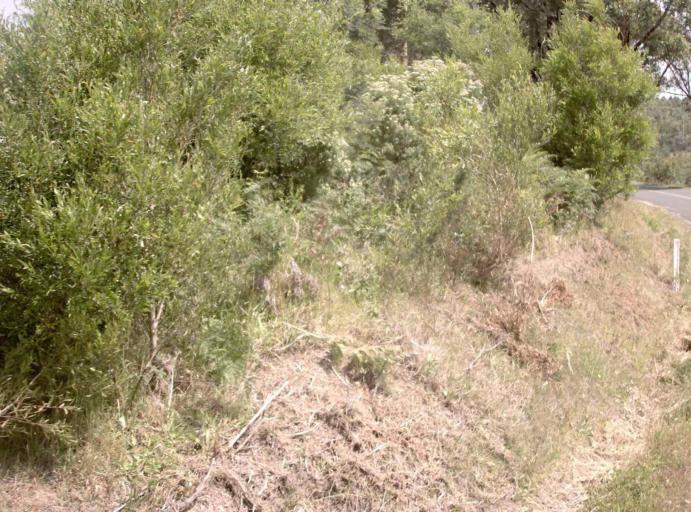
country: AU
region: Victoria
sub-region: Latrobe
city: Traralgon
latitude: -38.3579
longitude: 146.5676
